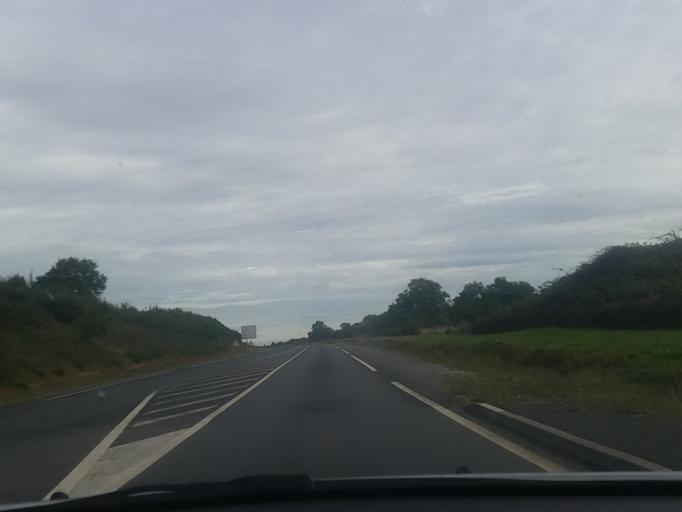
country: FR
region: Pays de la Loire
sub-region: Departement de la Loire-Atlantique
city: Chateaubriant
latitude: 47.7010
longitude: -1.3656
